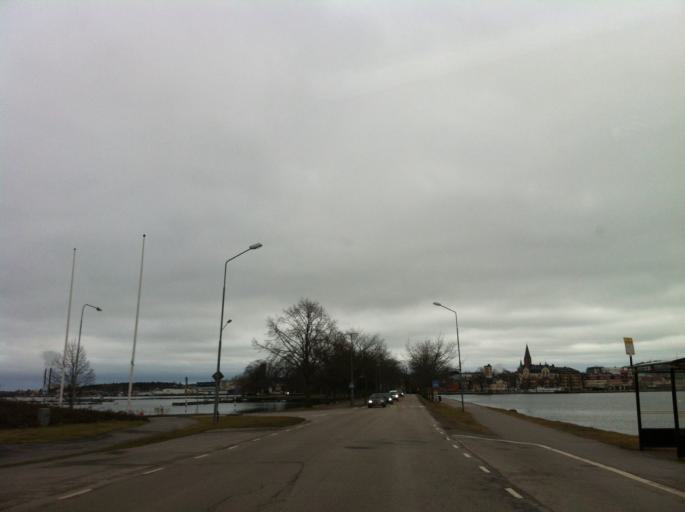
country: SE
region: Kalmar
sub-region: Vasterviks Kommun
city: Vaestervik
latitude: 57.8025
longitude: 16.6076
